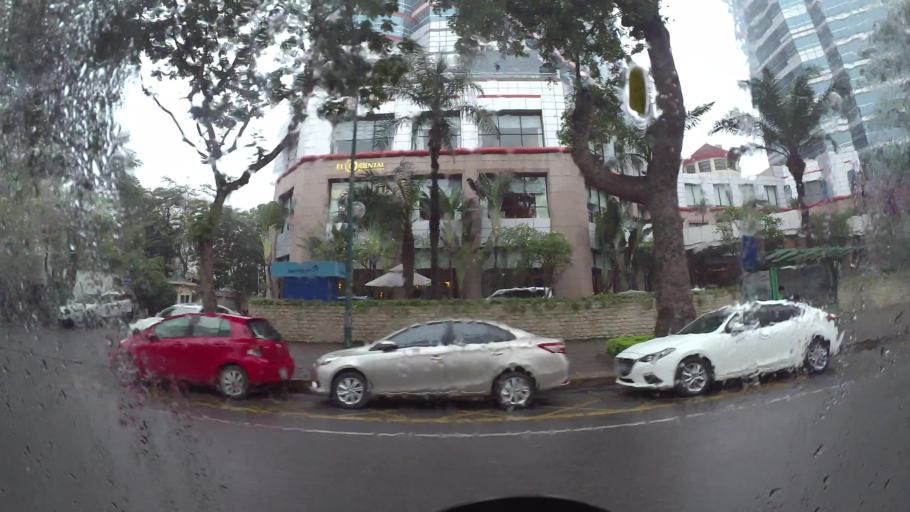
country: VN
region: Ha Noi
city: Hoan Kiem
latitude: 21.0241
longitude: 105.8480
